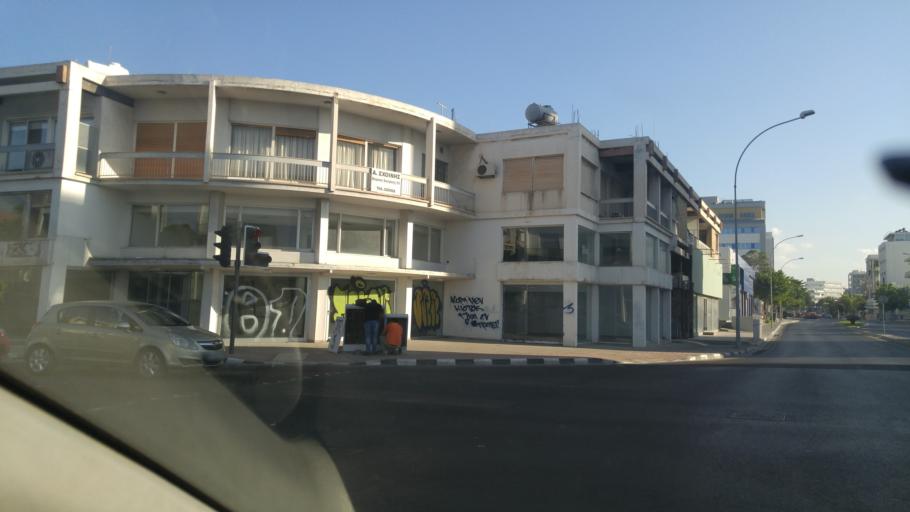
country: CY
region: Limassol
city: Limassol
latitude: 34.6834
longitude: 33.0303
